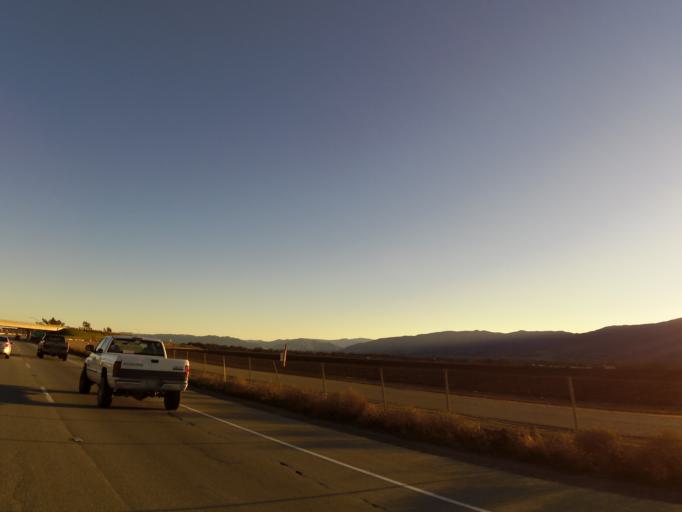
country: US
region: California
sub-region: Monterey County
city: Soledad
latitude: 36.4212
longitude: -121.3254
